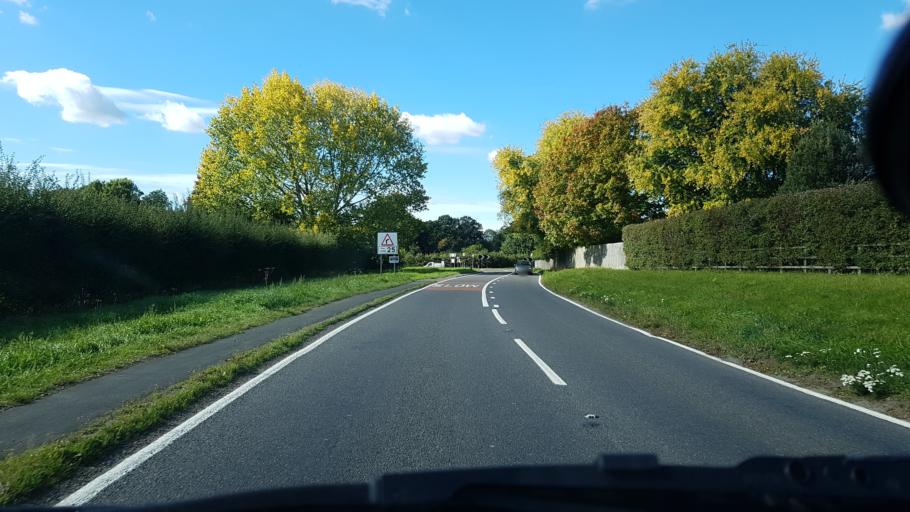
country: GB
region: England
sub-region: West Sussex
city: Billingshurst
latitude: 51.0202
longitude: -0.4709
